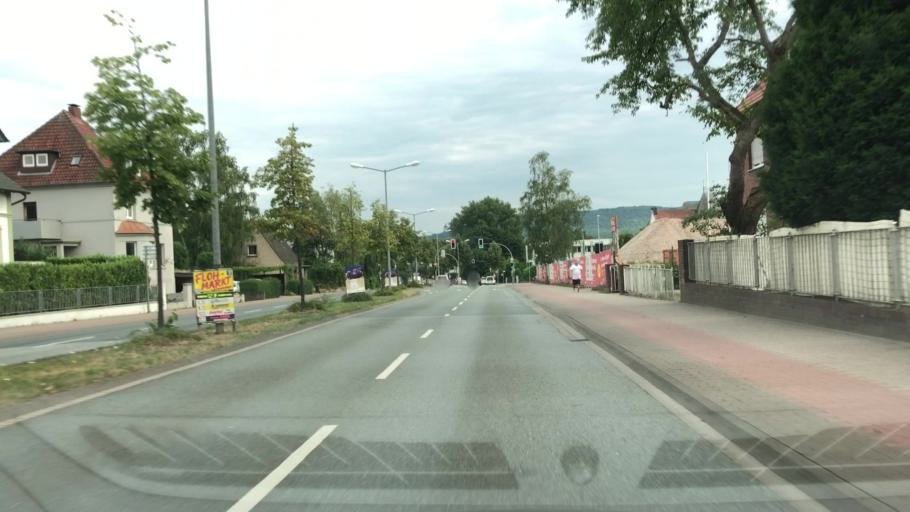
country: DE
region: North Rhine-Westphalia
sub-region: Regierungsbezirk Detmold
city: Minden
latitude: 52.2872
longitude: 8.9010
